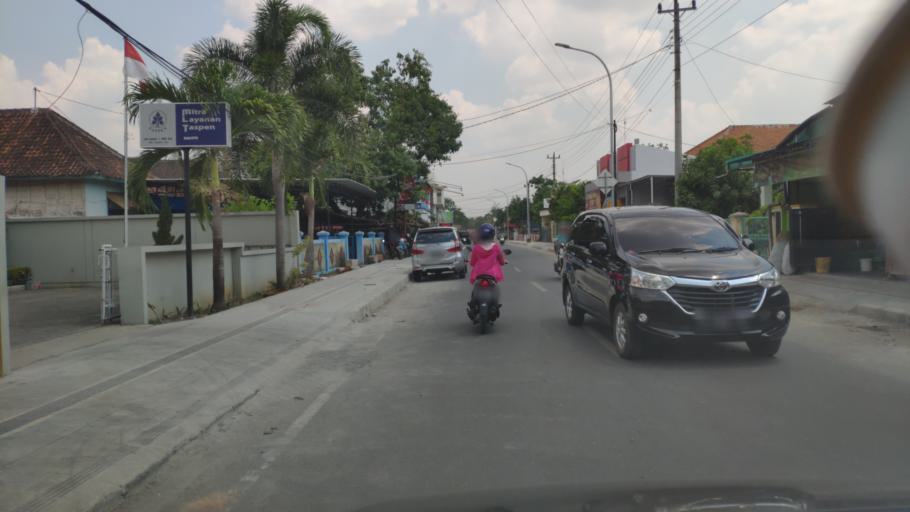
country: ID
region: Central Java
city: Mlangsen
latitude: -6.9732
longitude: 111.4136
